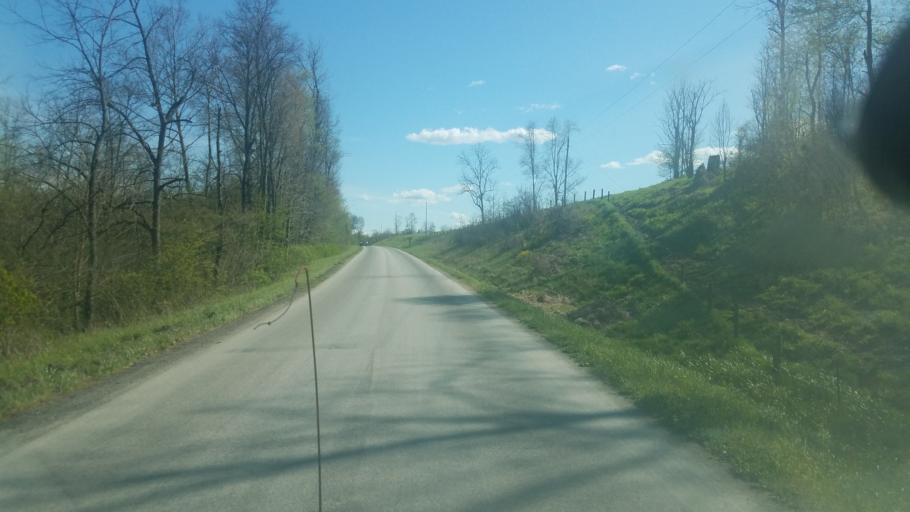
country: US
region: Ohio
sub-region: Coshocton County
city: Coshocton
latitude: 40.4167
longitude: -81.8322
